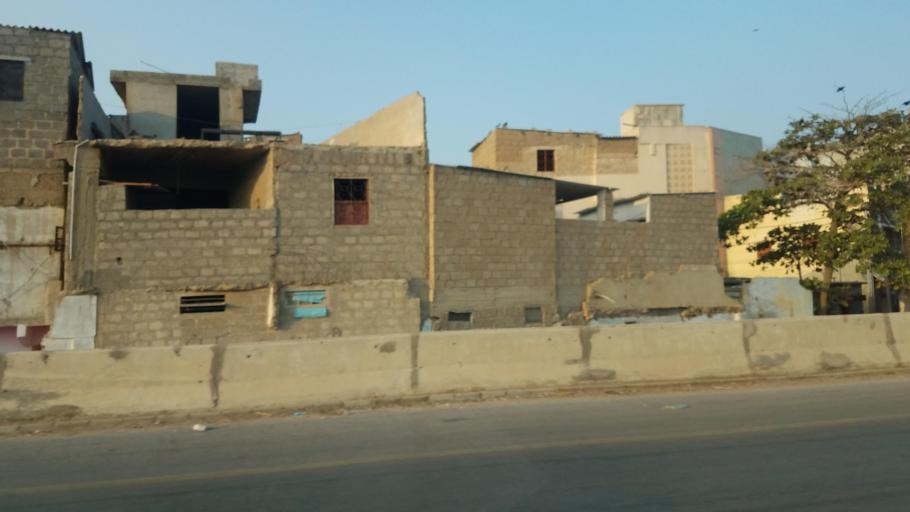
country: PK
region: Sindh
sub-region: Karachi District
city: Karachi
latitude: 24.8941
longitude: 67.0383
